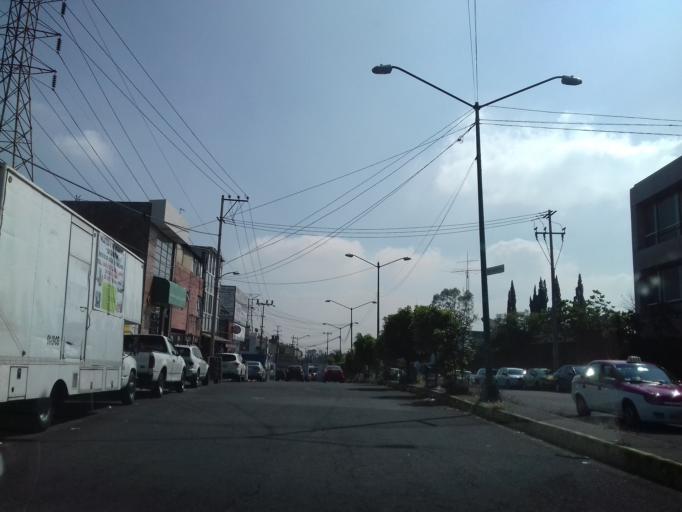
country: MX
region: Mexico City
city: Magdalena Contreras
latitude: 19.3333
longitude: -99.2000
